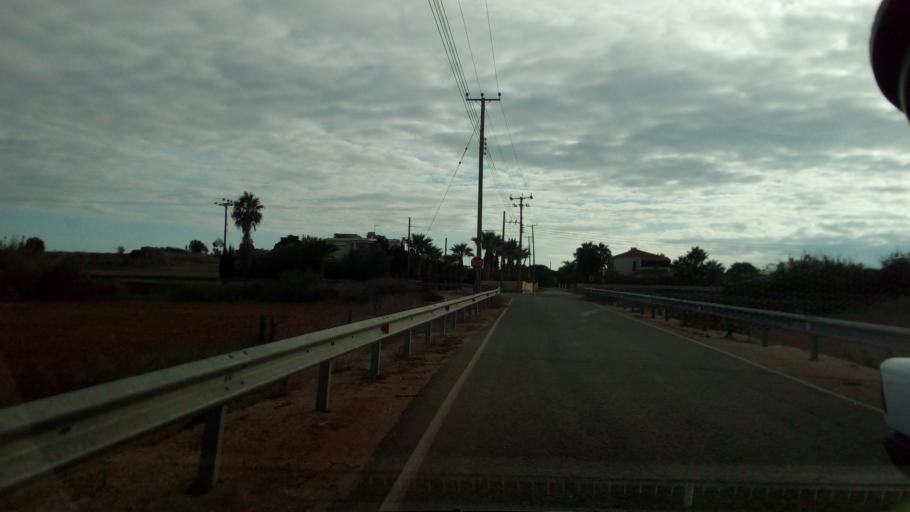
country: CY
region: Ammochostos
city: Liopetri
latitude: 35.0425
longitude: 33.8875
